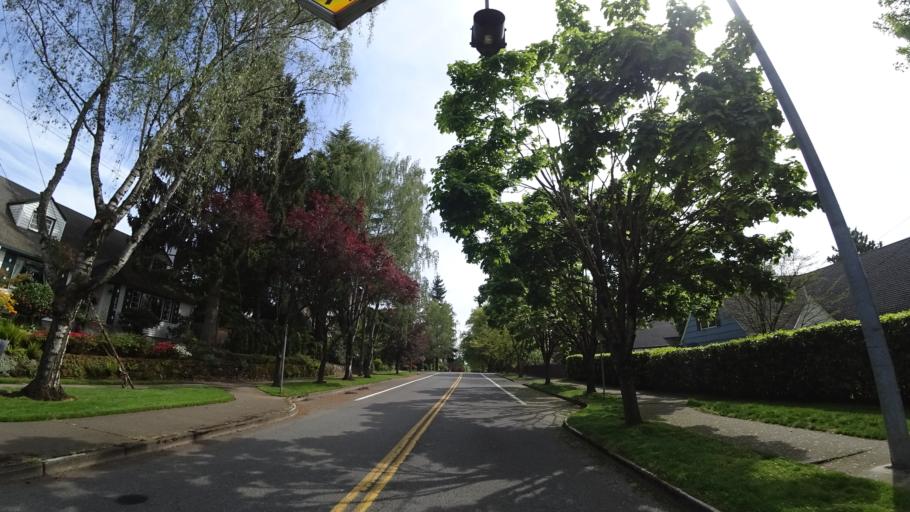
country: US
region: Oregon
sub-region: Clackamas County
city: Milwaukie
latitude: 45.4747
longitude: -122.6227
